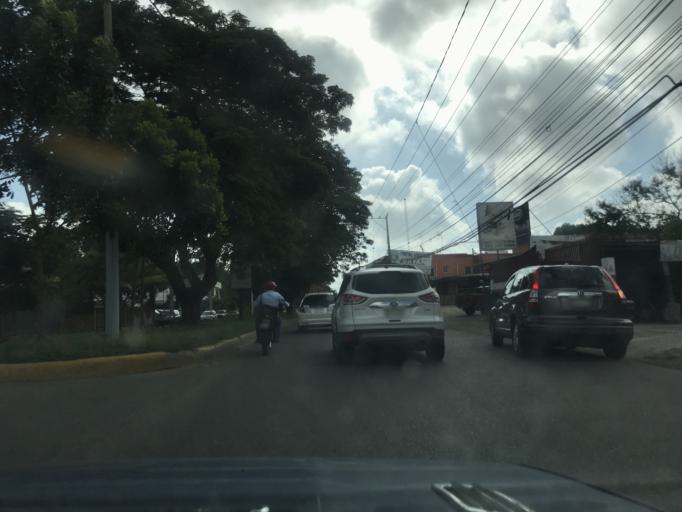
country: DO
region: Santiago
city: Santiago de los Caballeros
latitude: 19.4397
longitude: -70.7187
